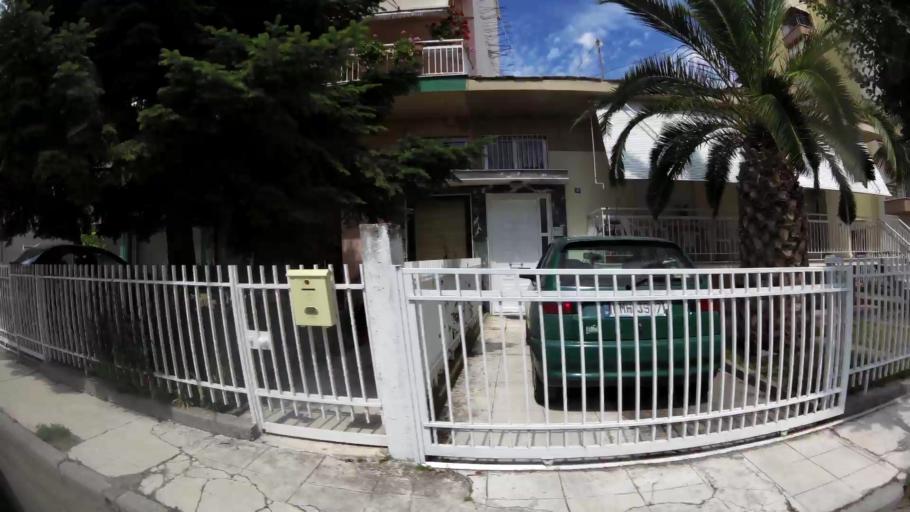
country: GR
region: Central Macedonia
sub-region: Nomos Pierias
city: Katerini
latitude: 40.2750
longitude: 22.4992
